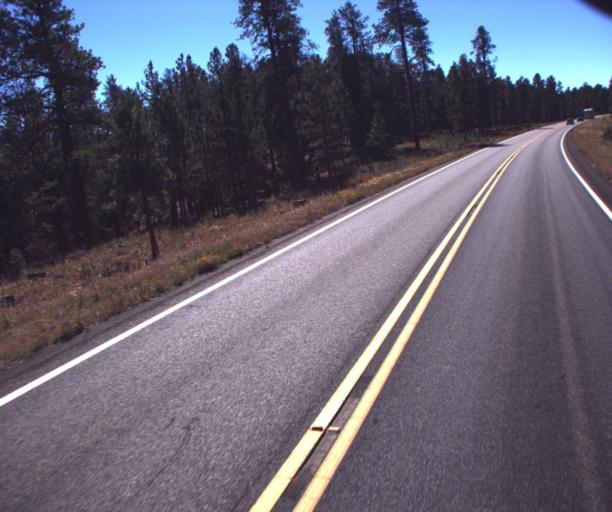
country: US
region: Arizona
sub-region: Coconino County
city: Fredonia
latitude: 36.6948
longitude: -112.2140
